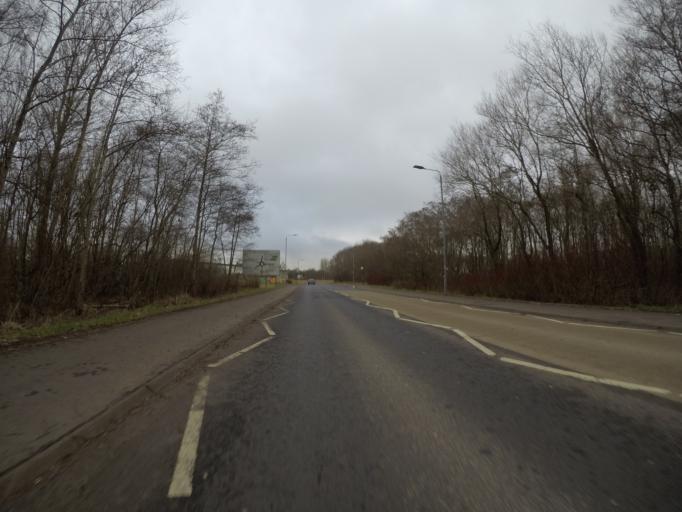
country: GB
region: Scotland
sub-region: North Ayrshire
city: Irvine
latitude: 55.6316
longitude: -4.6433
